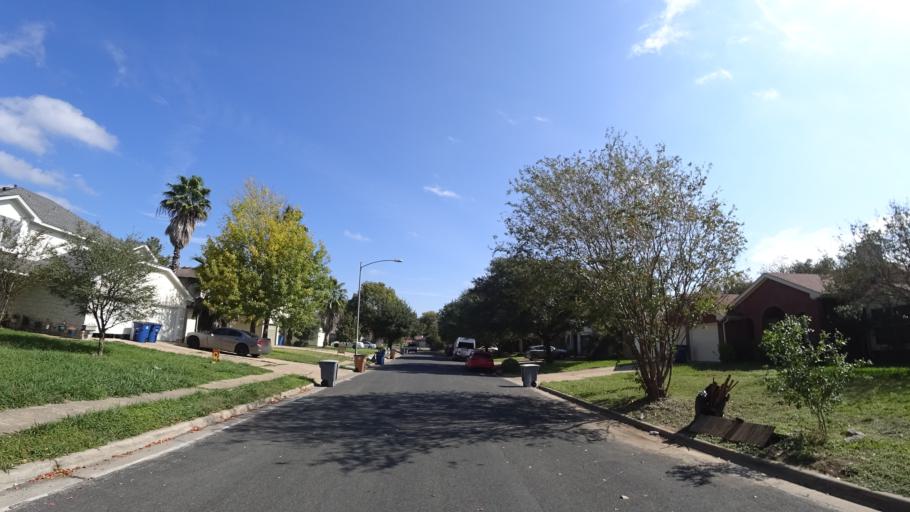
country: US
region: Texas
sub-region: Travis County
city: Shady Hollow
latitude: 30.1971
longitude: -97.8268
